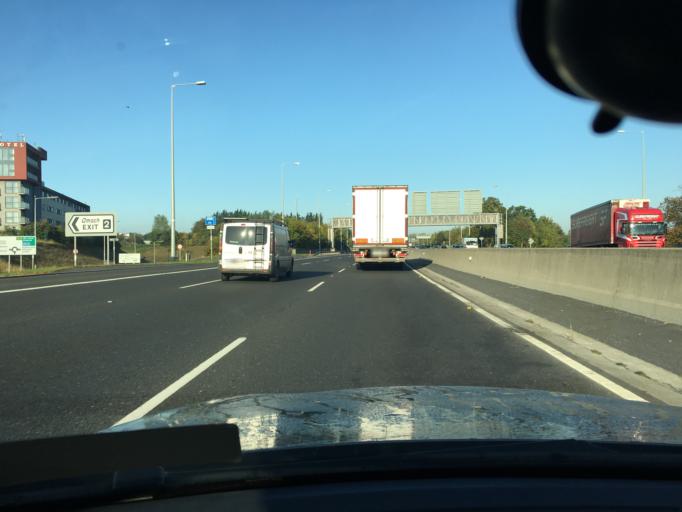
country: IE
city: Palmerstown
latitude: 53.3555
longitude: -6.3987
